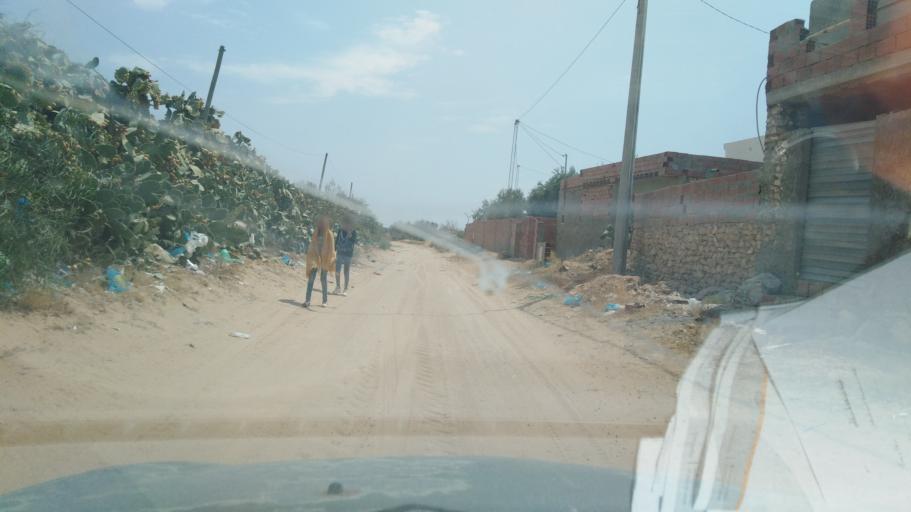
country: TN
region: Safaqis
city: Sfax
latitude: 34.7392
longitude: 10.5422
